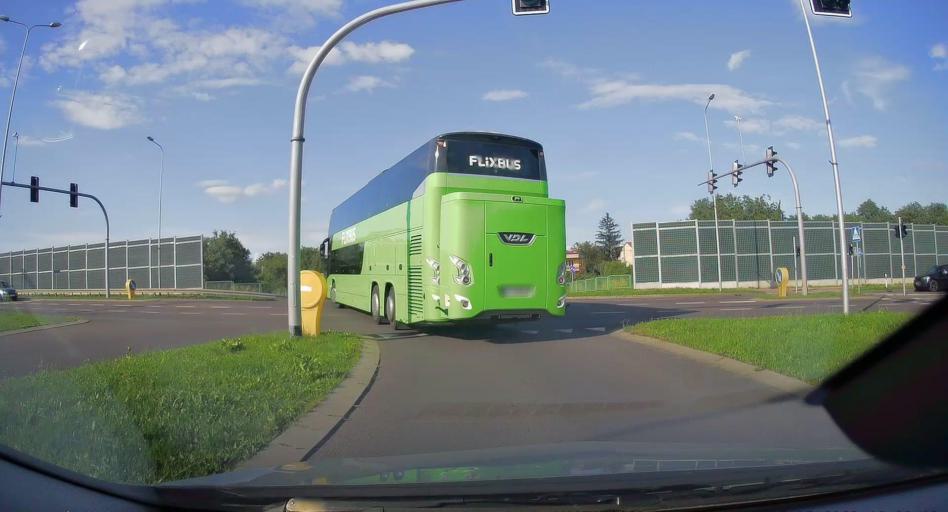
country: PL
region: Subcarpathian Voivodeship
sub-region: Przemysl
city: Przemysl
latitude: 49.7950
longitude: 22.7876
